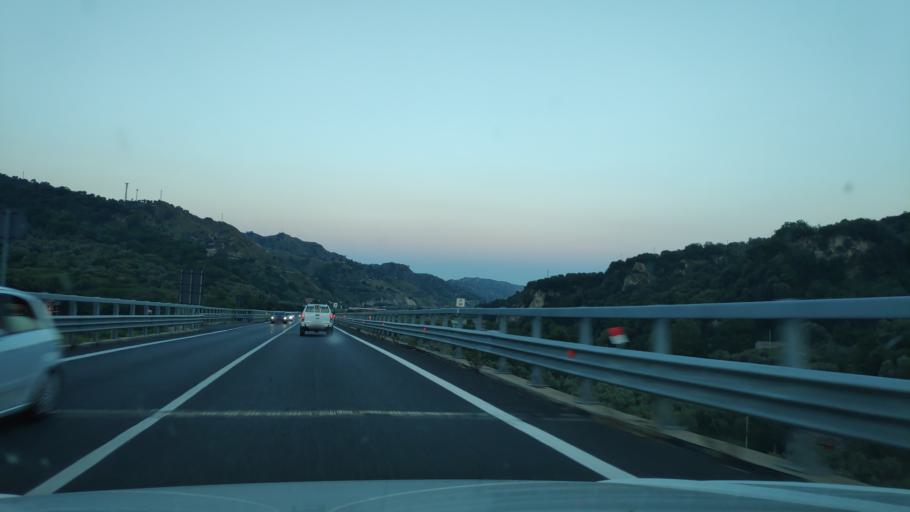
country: IT
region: Calabria
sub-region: Provincia di Reggio Calabria
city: Mammola
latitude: 38.3589
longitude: 16.2188
